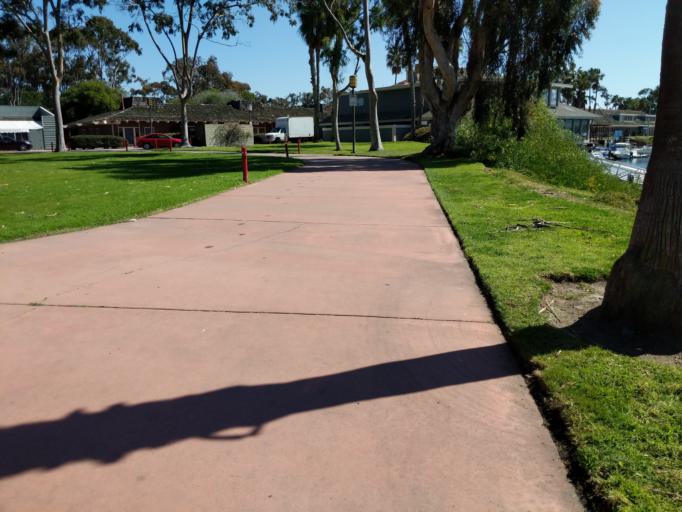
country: US
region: California
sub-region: San Diego County
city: San Diego
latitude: 32.7626
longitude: -117.2352
